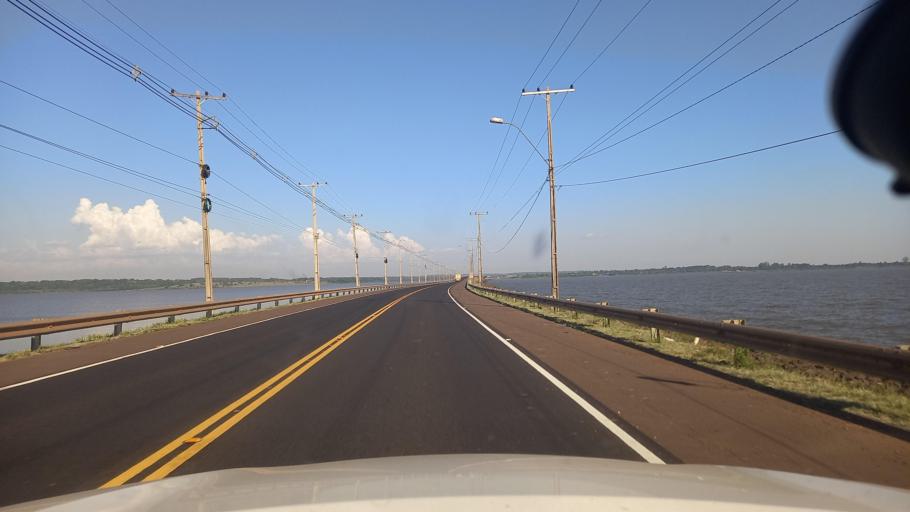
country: PY
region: Itapua
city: Carmen del Parana
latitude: -27.2017
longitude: -56.1771
